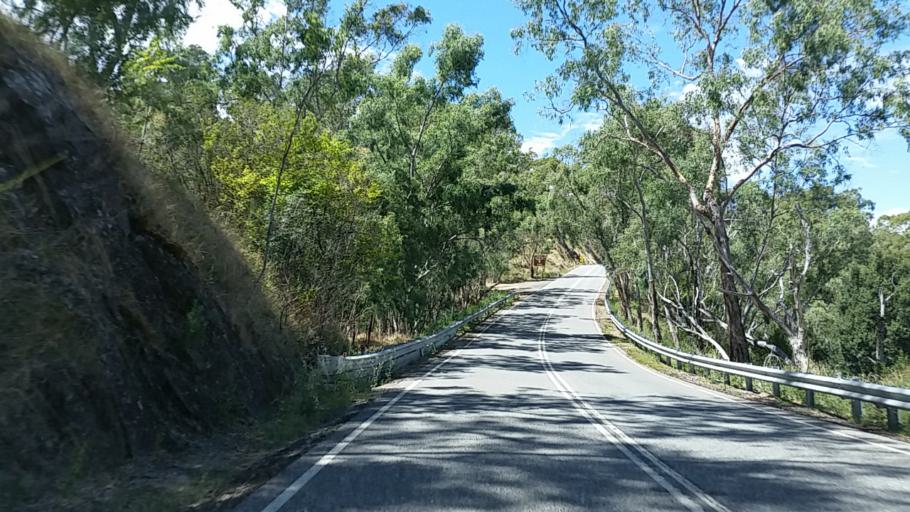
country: AU
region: South Australia
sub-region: Tea Tree Gully
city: Golden Grove
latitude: -34.8498
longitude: 138.7924
